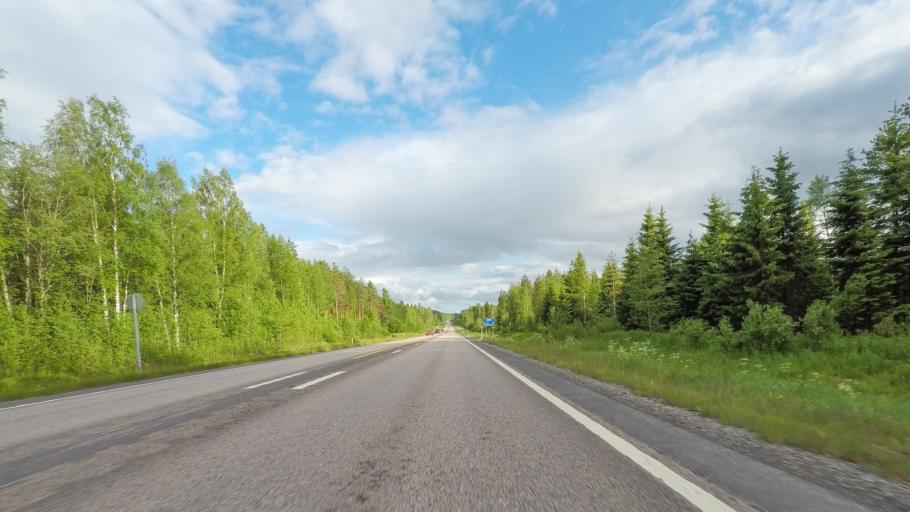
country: FI
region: Paijanne Tavastia
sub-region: Lahti
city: Hartola
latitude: 61.4035
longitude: 26.0453
